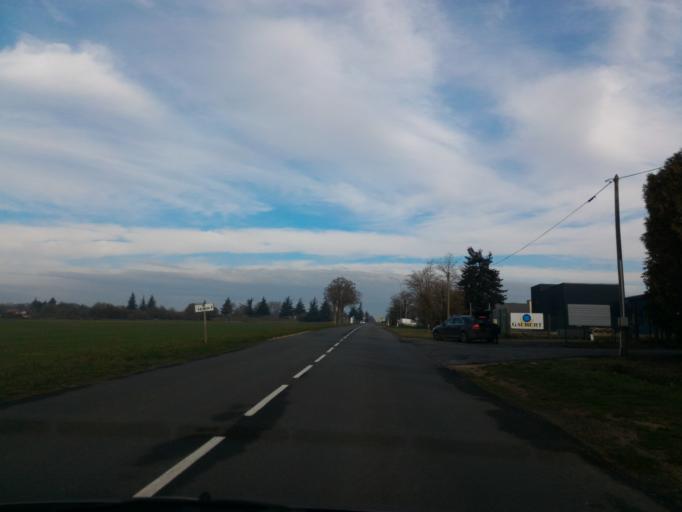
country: FR
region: Poitou-Charentes
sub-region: Departement de la Charente
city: Ruffec
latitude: 46.0426
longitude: 0.1978
